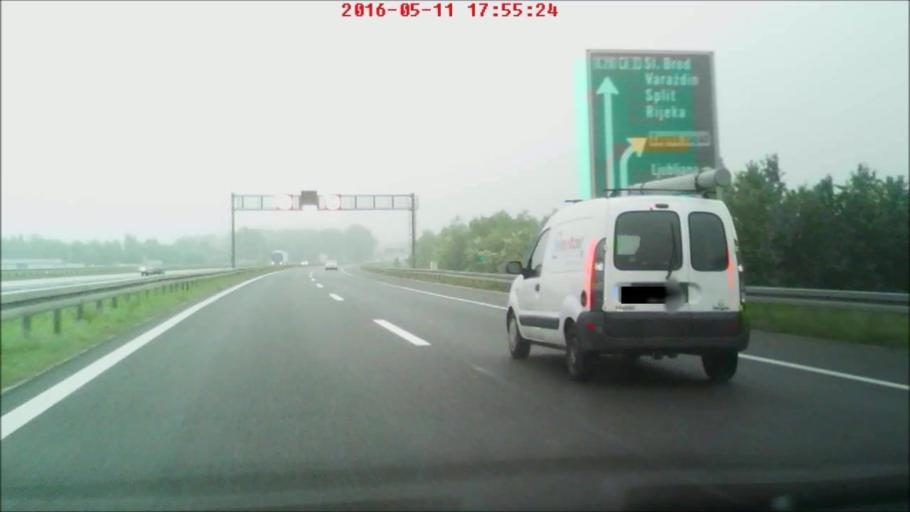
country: HR
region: Grad Zagreb
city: Jezdovec
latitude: 45.7985
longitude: 15.8425
